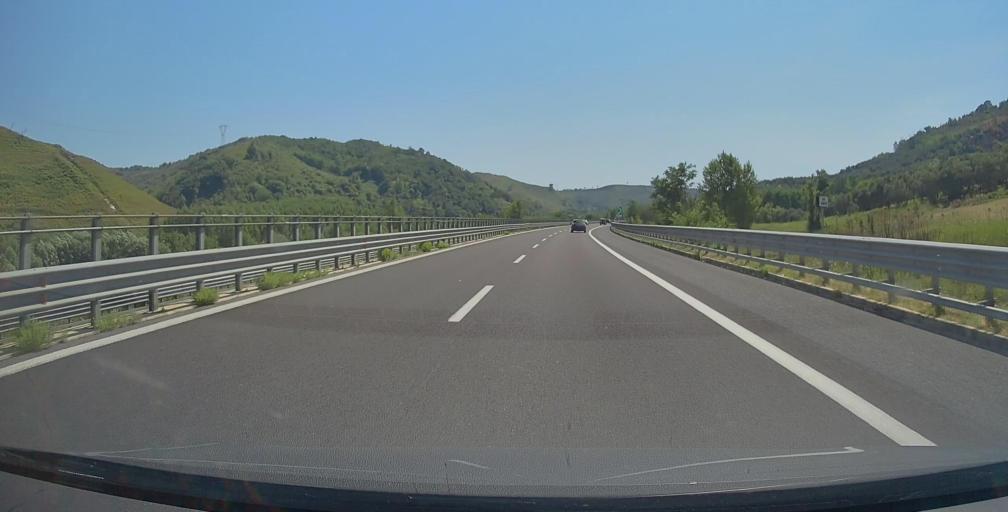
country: IT
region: Calabria
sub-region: Provincia di Vibo-Valentia
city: Francica
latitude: 38.5837
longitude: 16.1334
